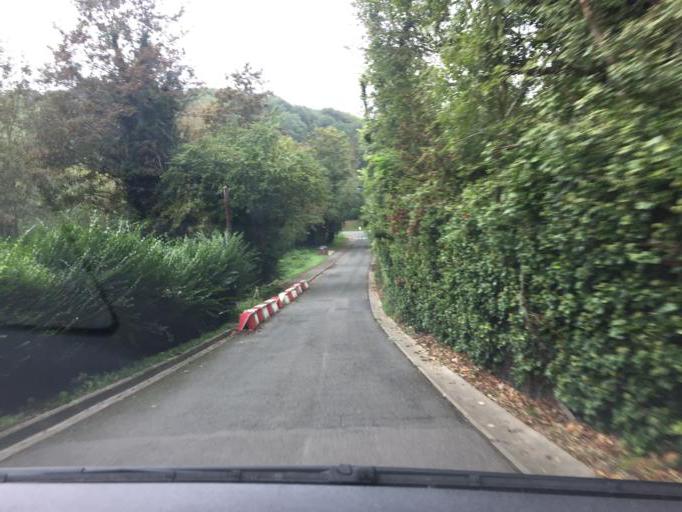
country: FR
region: Ile-de-France
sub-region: Departement de l'Essonne
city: Villiers-le-Bacle
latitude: 48.7222
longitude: 2.1252
